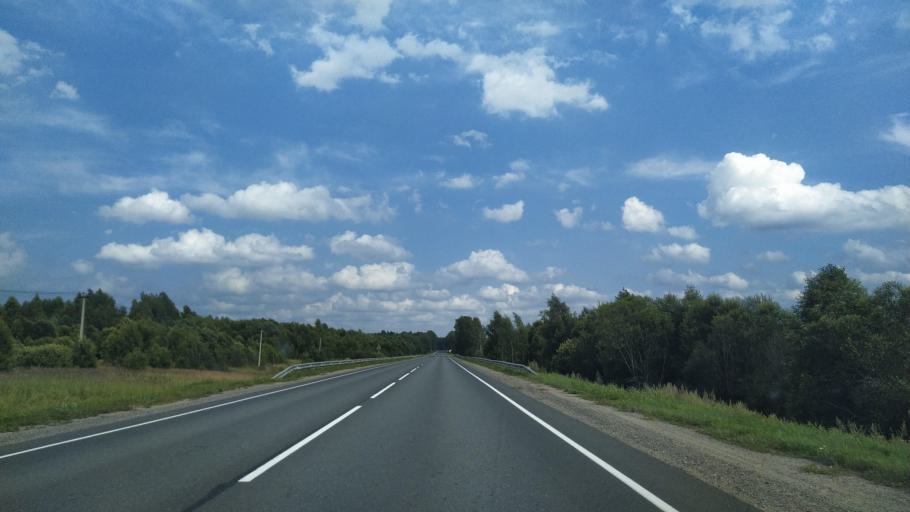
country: RU
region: Pskov
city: Dno
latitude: 57.9833
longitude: 29.7678
